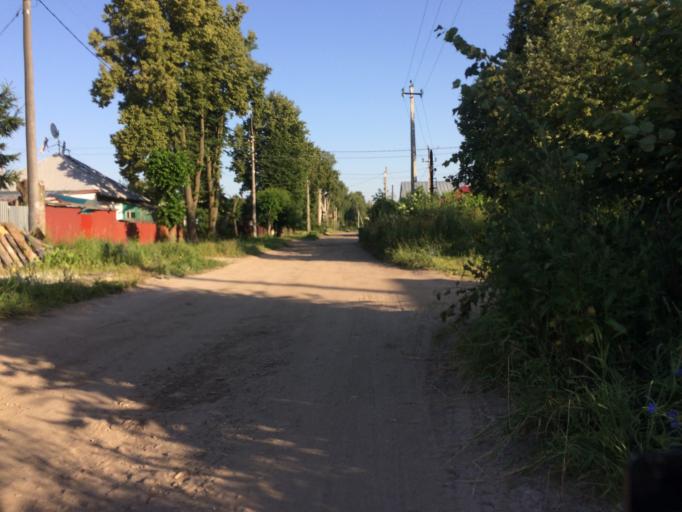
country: RU
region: Mariy-El
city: Yoshkar-Ola
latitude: 56.6493
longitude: 47.9094
